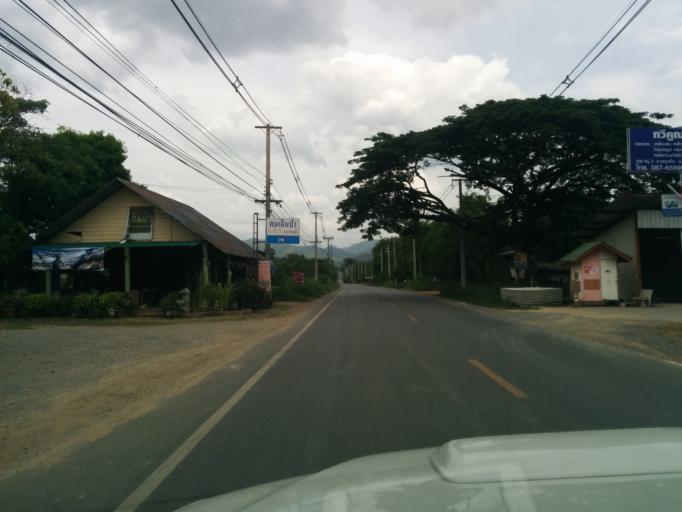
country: TH
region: Sara Buri
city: Muak Lek
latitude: 14.6173
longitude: 101.2123
